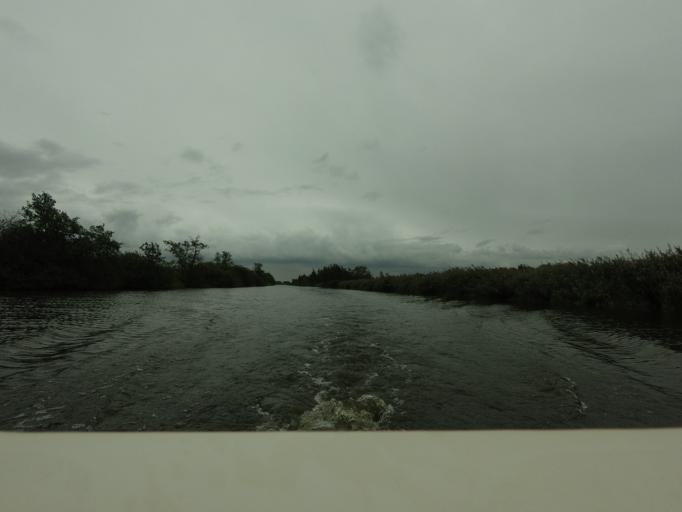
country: NL
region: Friesland
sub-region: Gemeente Boarnsterhim
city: Warten
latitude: 53.1199
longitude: 5.9303
